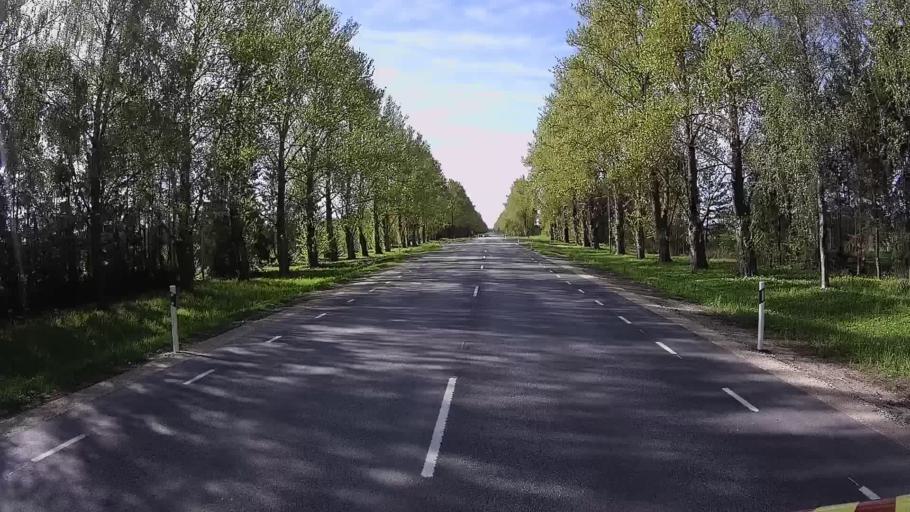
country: EE
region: Polvamaa
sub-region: Polva linn
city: Polva
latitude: 58.3006
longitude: 27.0012
